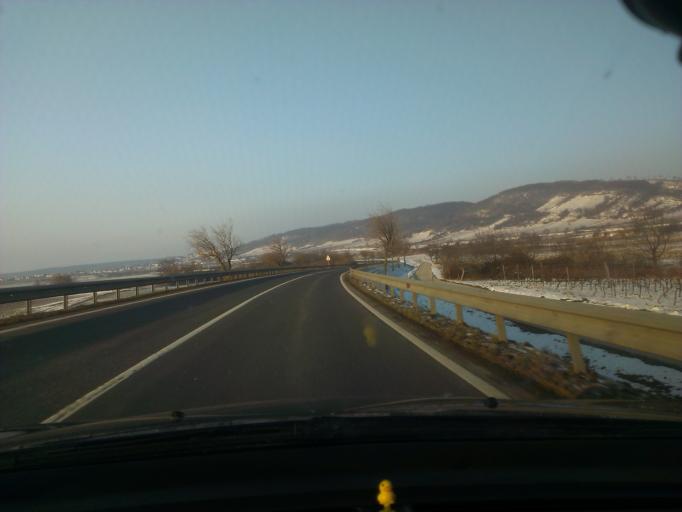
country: AT
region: Burgenland
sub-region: Eisenstadt-Umgebung
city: Donnerskirchen
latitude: 47.9079
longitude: 16.6688
